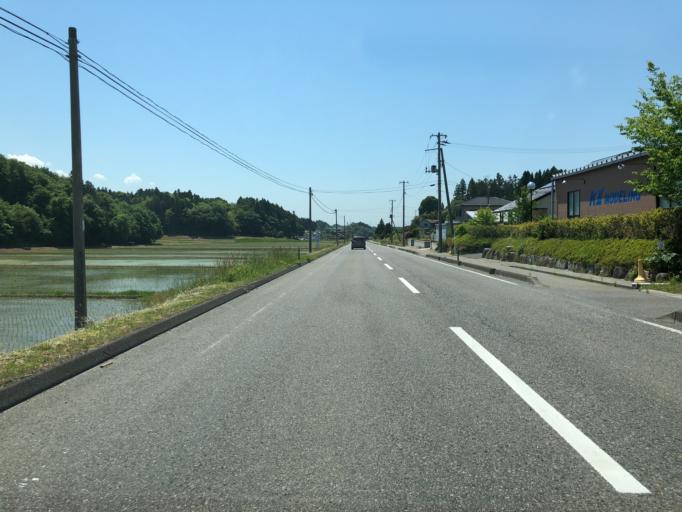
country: JP
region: Fukushima
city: Motomiya
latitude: 37.5066
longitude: 140.4580
